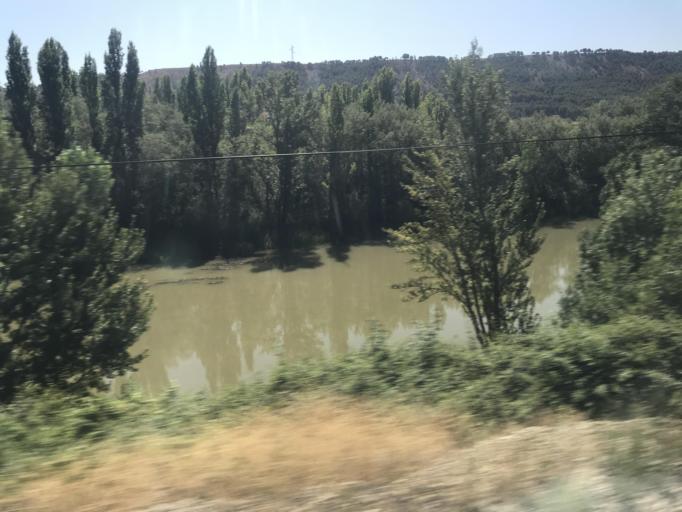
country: ES
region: Castille and Leon
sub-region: Provincia de Valladolid
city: Cabezon
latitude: 41.7501
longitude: -4.6385
